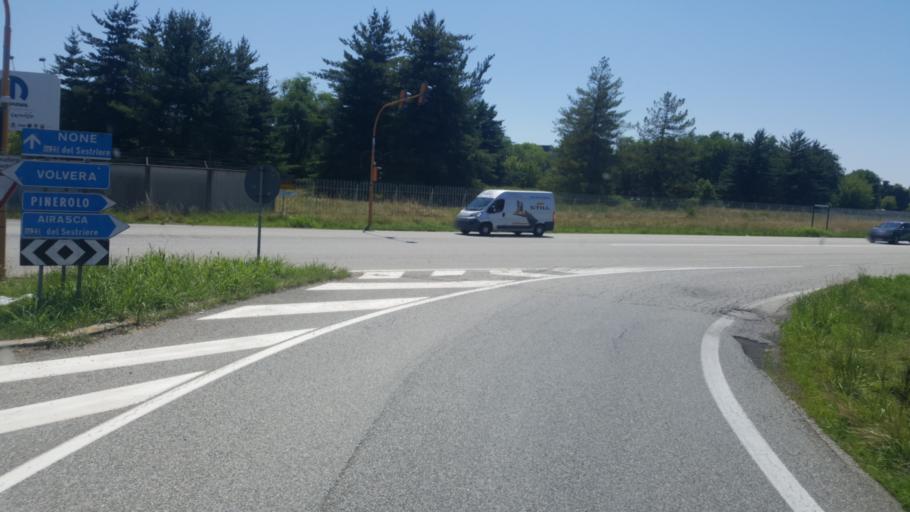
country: IT
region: Piedmont
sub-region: Provincia di Torino
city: Volvera
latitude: 44.9407
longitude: 7.5072
